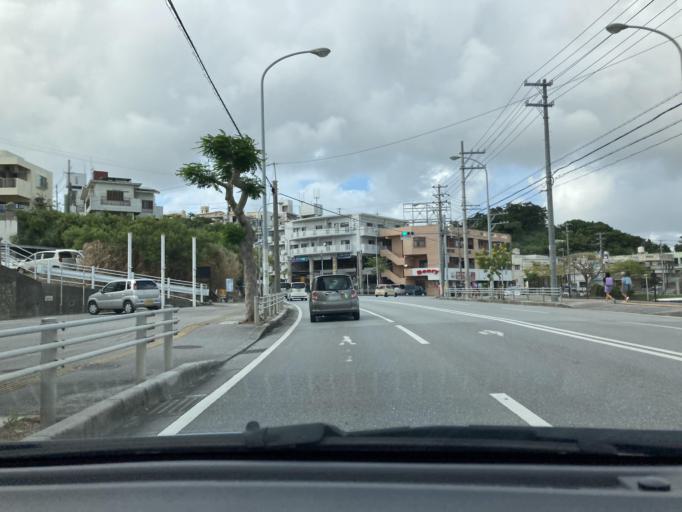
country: JP
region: Okinawa
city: Tomigusuku
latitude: 26.1812
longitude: 127.6811
